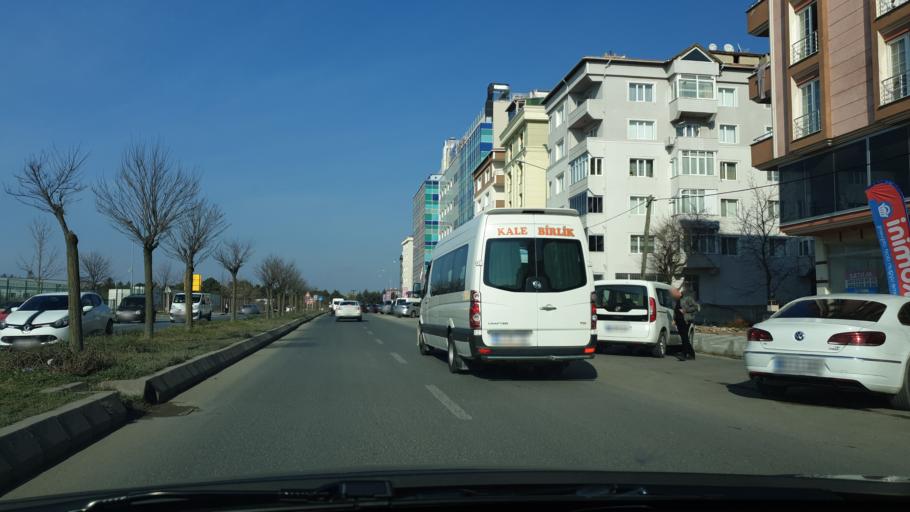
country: TR
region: Tekirdag
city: Cerkezkoey
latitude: 41.2926
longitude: 27.9941
